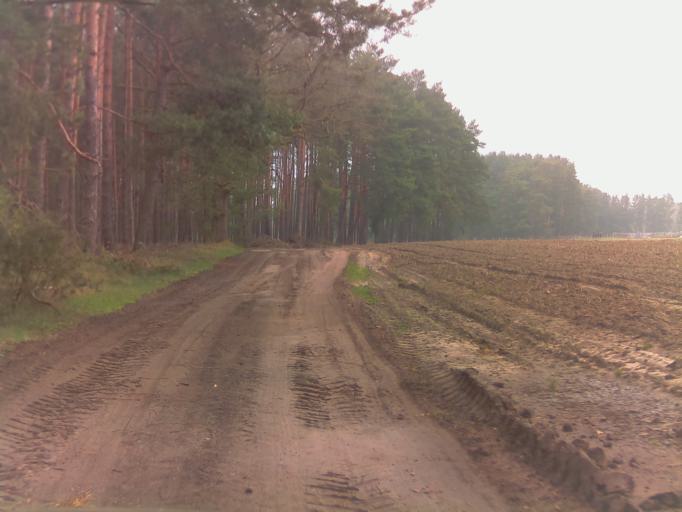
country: DE
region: Brandenburg
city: Neu Zauche
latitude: 51.9659
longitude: 14.1297
